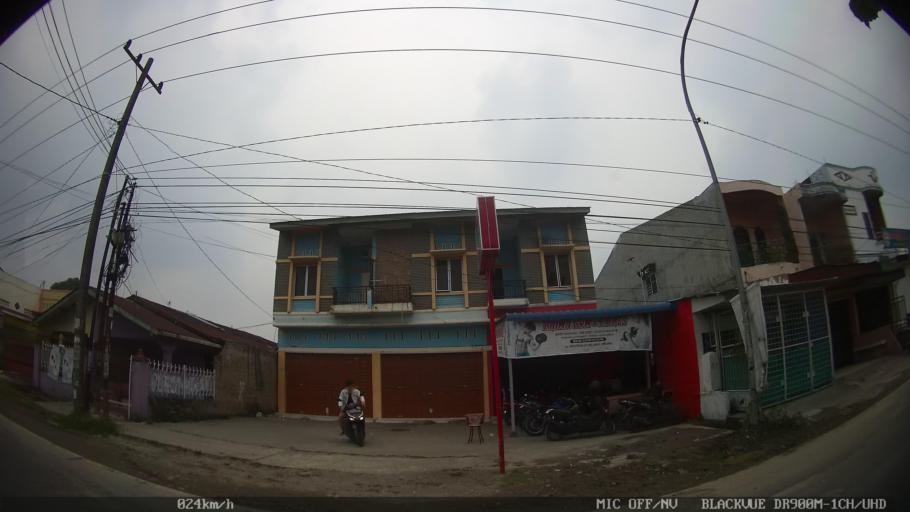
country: ID
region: North Sumatra
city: Medan
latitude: 3.5645
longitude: 98.7217
